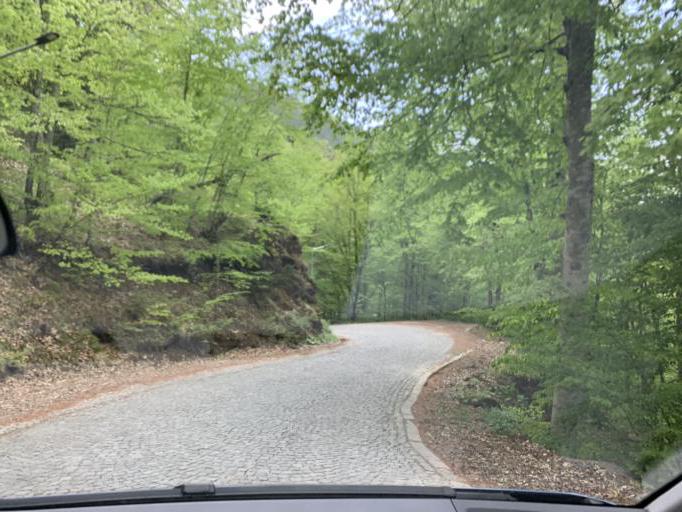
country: TR
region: Zonguldak
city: Egerci
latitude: 40.9359
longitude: 31.7413
